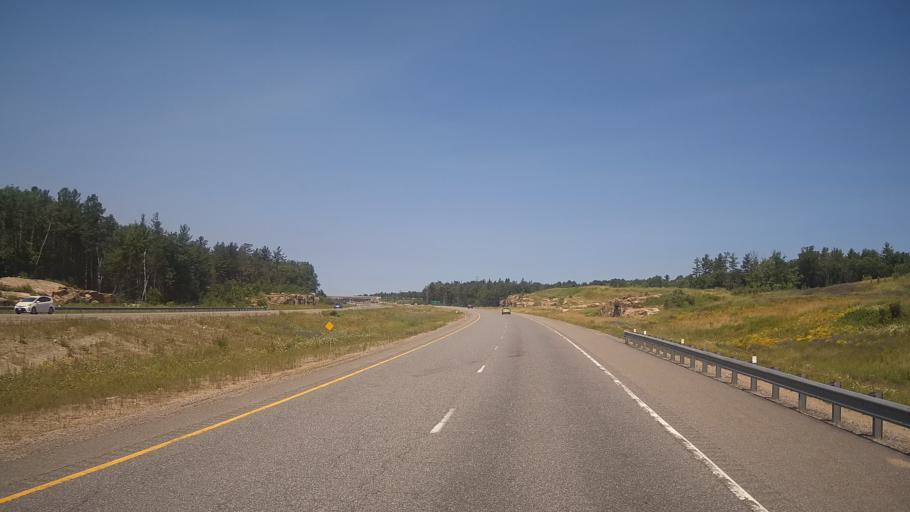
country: CA
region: Ontario
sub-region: Parry Sound District
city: Parry Sound
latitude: 45.4121
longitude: -80.0646
